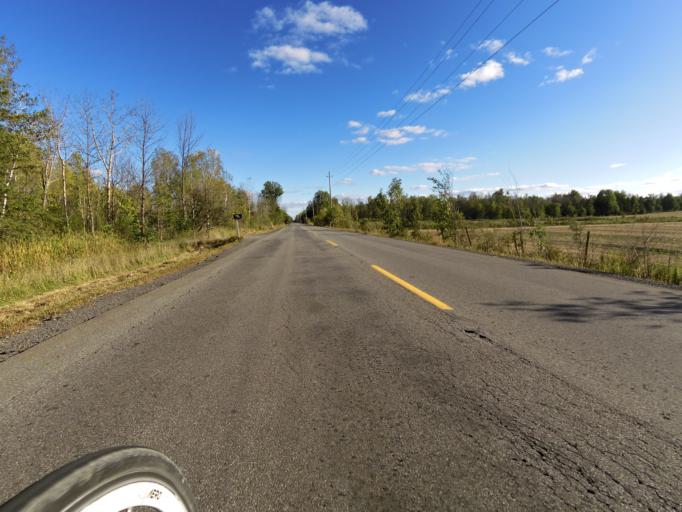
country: CA
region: Ontario
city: Bells Corners
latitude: 45.1749
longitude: -75.8027
